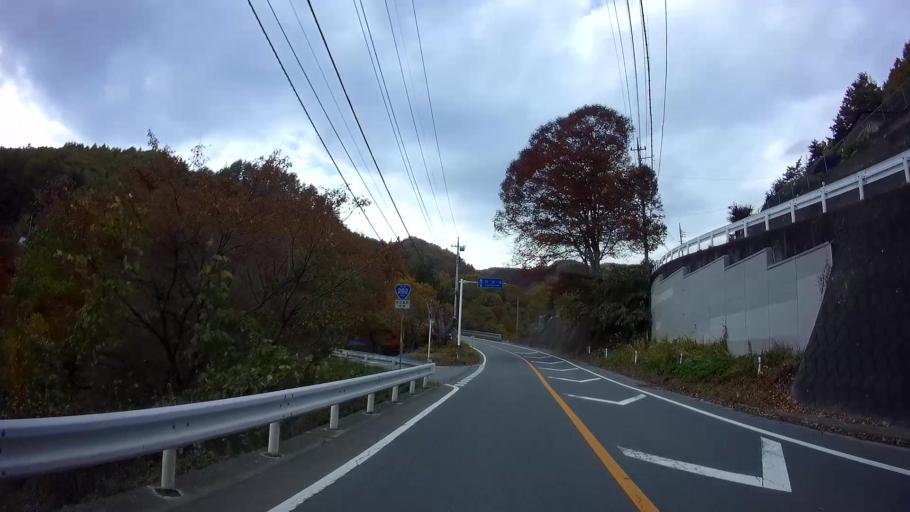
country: JP
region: Gunma
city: Nakanojomachi
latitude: 36.5688
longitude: 138.6350
